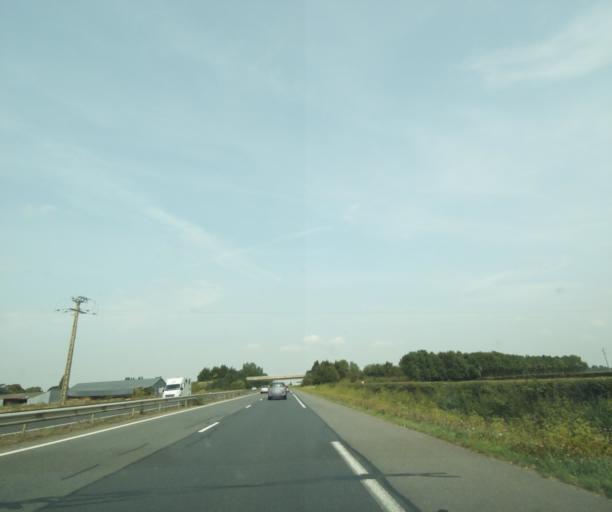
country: FR
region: Lower Normandy
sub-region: Departement du Calvados
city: Bretteville-sur-Laize
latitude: 49.0535
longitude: -0.2858
